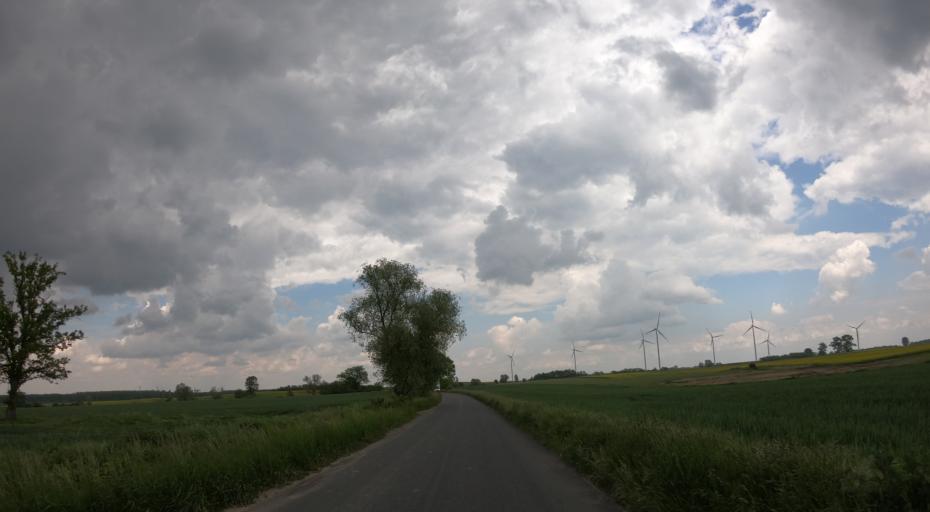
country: PL
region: West Pomeranian Voivodeship
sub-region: Powiat pyrzycki
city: Kozielice
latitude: 53.1382
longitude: 14.7600
